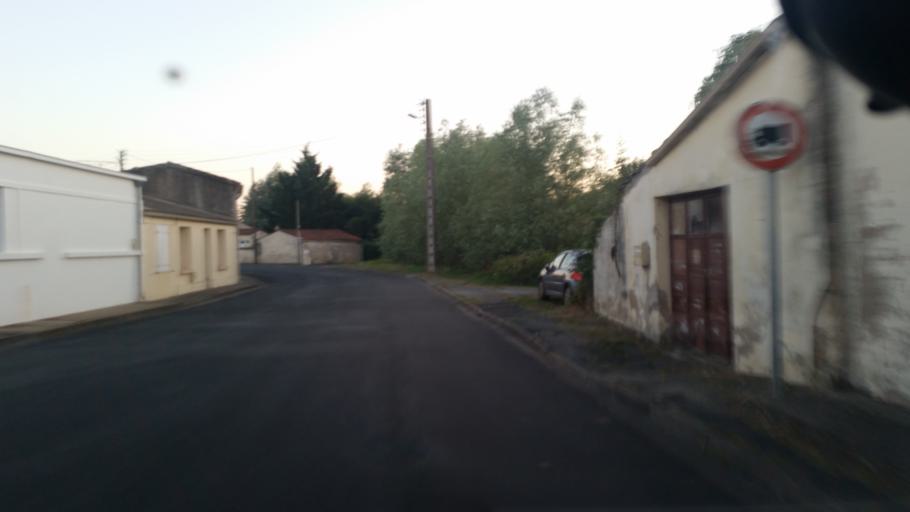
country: FR
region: Poitou-Charentes
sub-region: Departement de la Charente-Maritime
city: Marans
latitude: 46.3116
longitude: -0.9985
